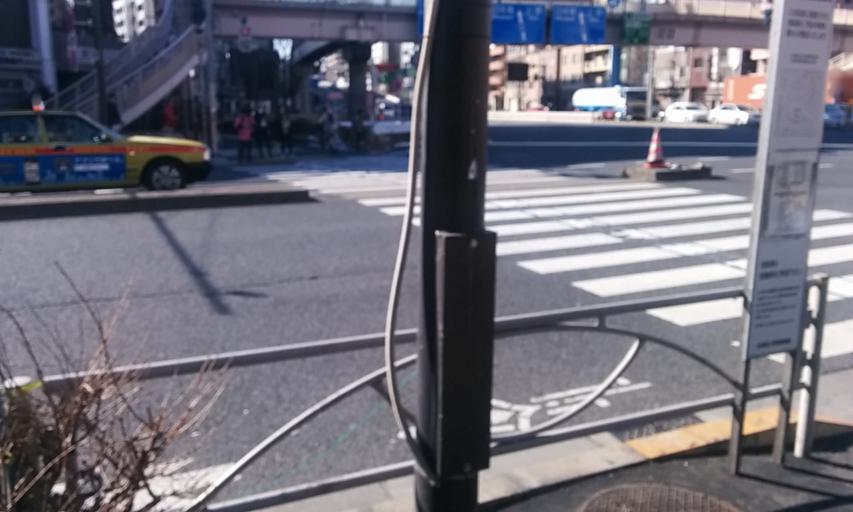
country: JP
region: Tokyo
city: Tokyo
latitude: 35.7198
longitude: 139.7842
